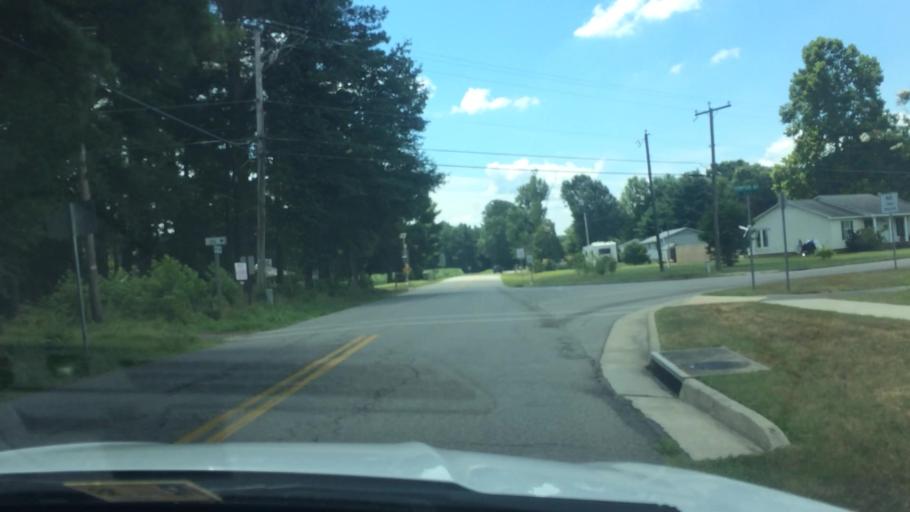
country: US
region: Virginia
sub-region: King William County
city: West Point
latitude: 37.5582
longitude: -76.7941
